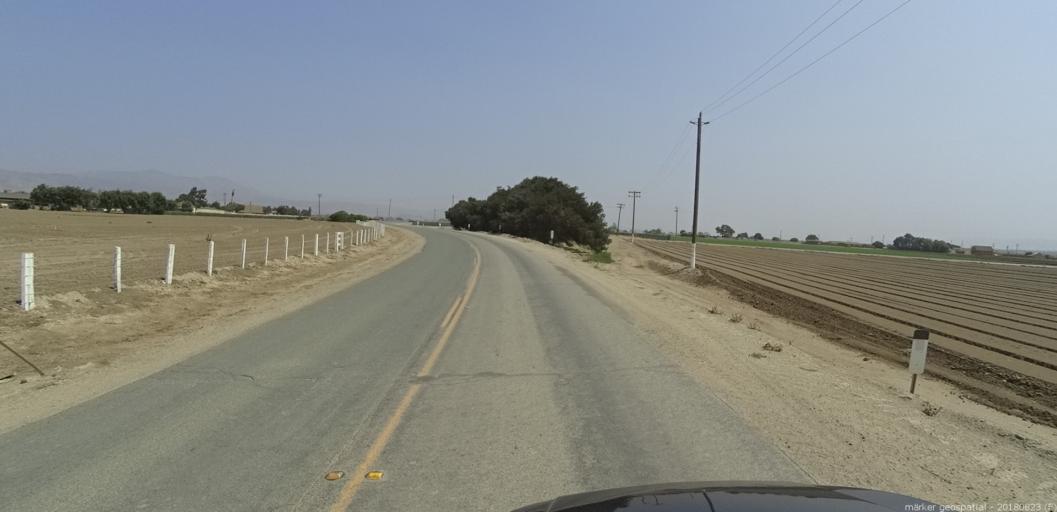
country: US
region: California
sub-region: Monterey County
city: Soledad
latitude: 36.4039
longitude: -121.3496
